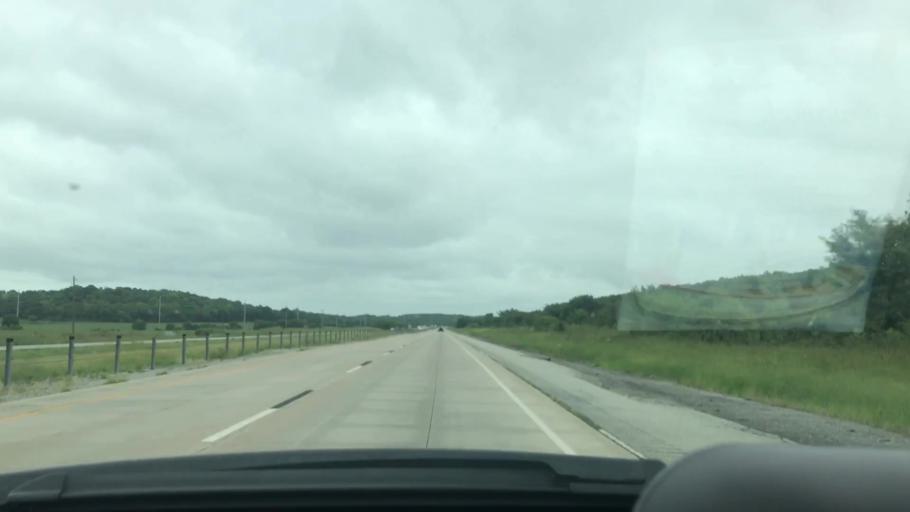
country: US
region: Oklahoma
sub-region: Atoka County
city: Atoka
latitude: 34.5508
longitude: -96.0224
